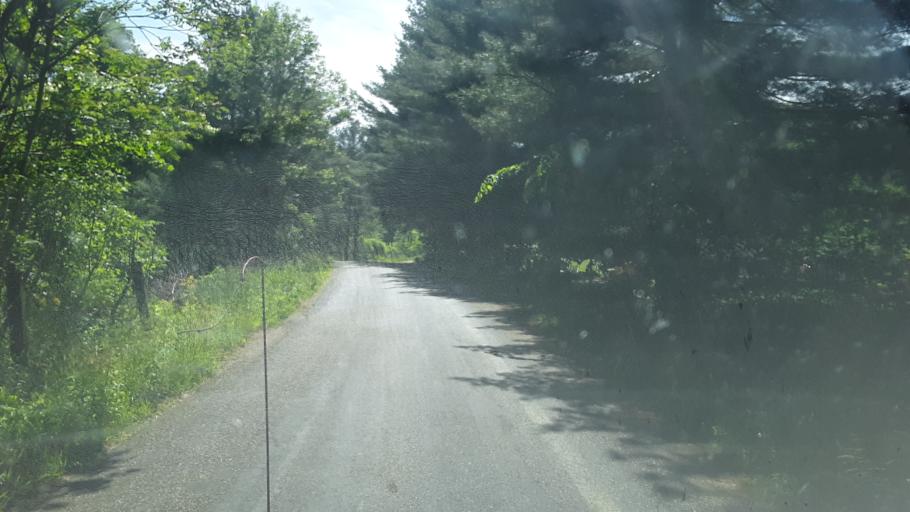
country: US
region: Ohio
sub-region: Coshocton County
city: West Lafayette
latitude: 40.2416
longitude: -81.7075
